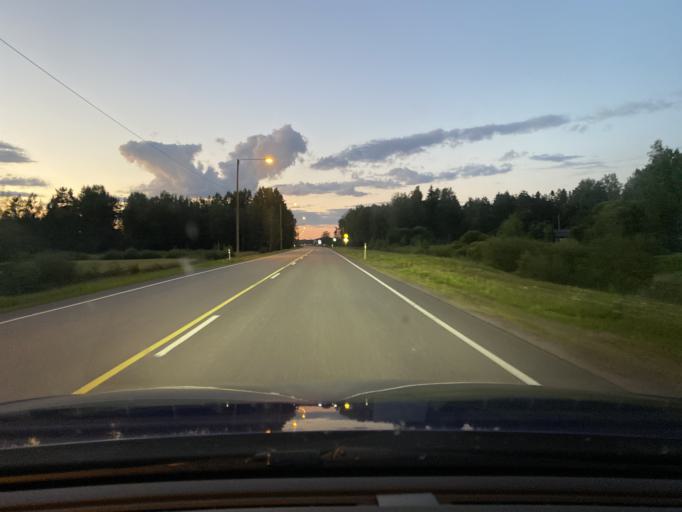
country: FI
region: Varsinais-Suomi
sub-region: Loimaa
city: Oripaeae
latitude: 60.8581
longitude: 22.6920
